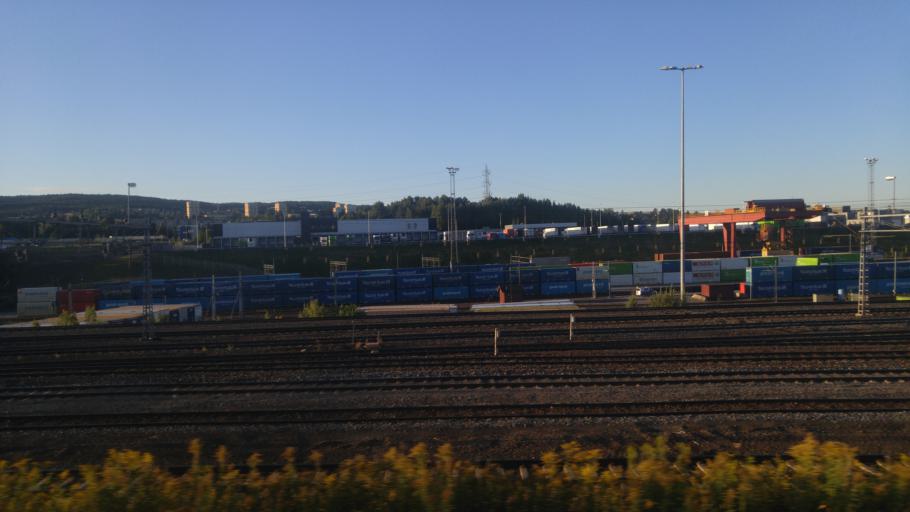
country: NO
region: Akershus
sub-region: Lorenskog
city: Kjenn
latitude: 59.9396
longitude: 10.8539
